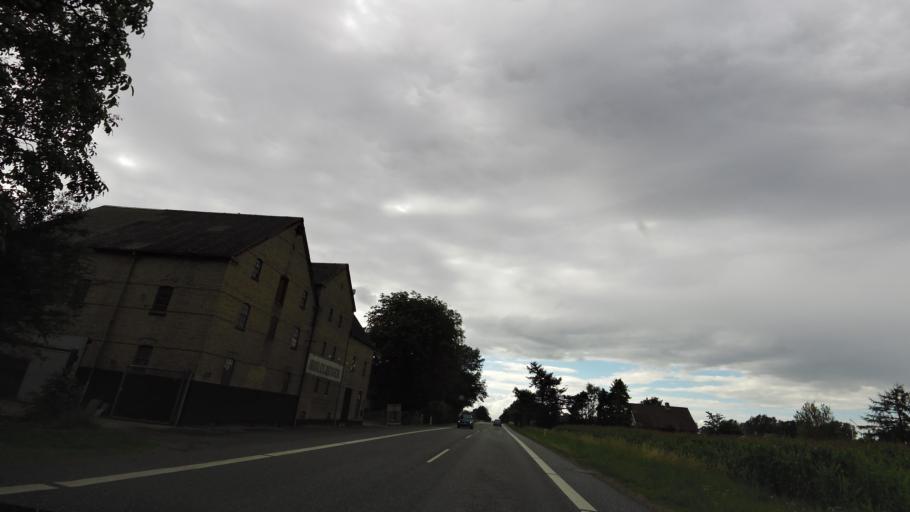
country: DK
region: South Denmark
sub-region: Middelfart Kommune
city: Norre Aby
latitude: 55.4650
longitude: 9.9154
